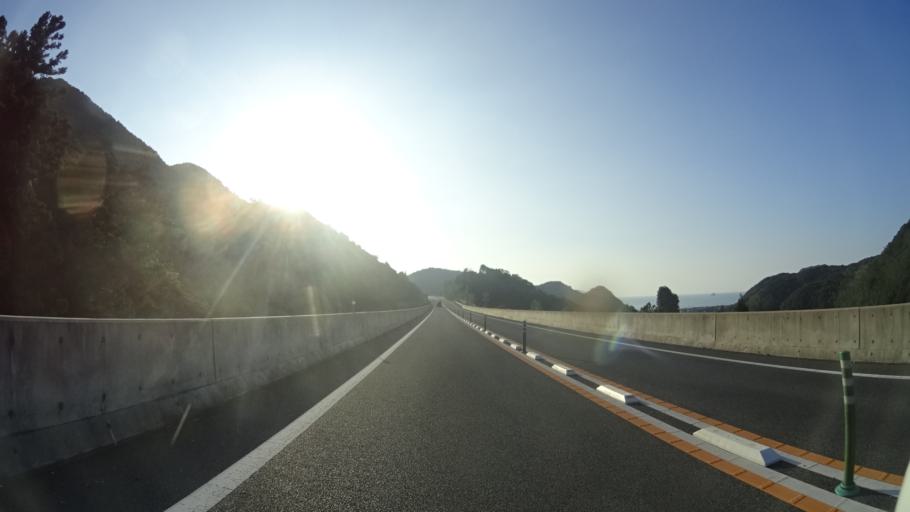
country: JP
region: Yamaguchi
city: Hagi
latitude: 34.3877
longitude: 131.3386
